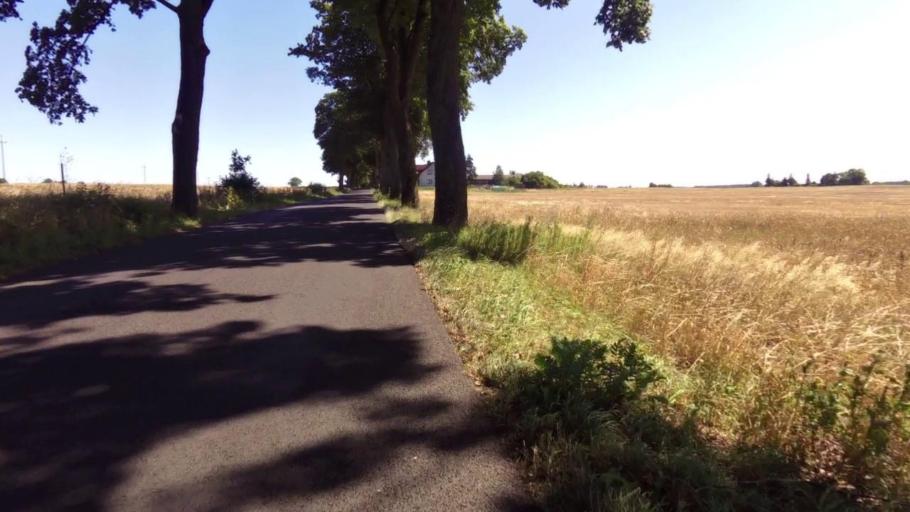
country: PL
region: West Pomeranian Voivodeship
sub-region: Powiat drawski
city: Czaplinek
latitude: 53.5617
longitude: 16.2685
